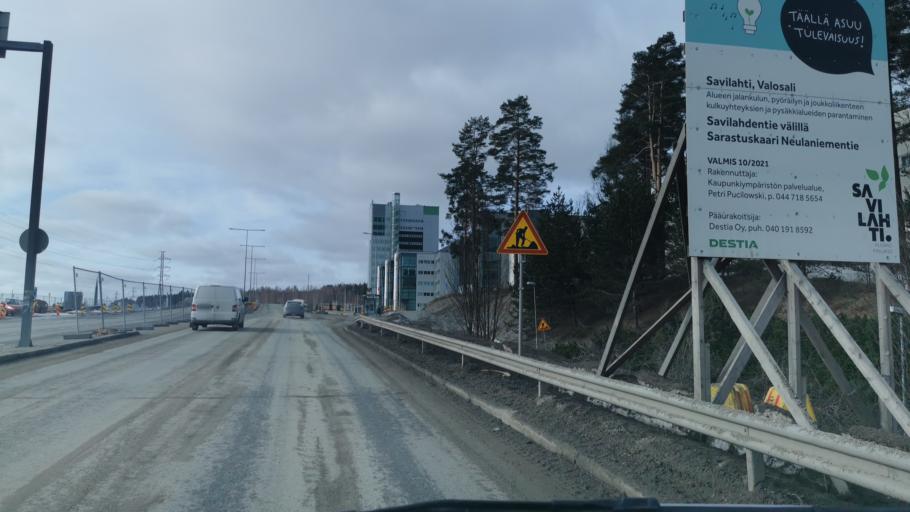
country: FI
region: Northern Savo
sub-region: Kuopio
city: Kuopio
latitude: 62.8901
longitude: 27.6337
